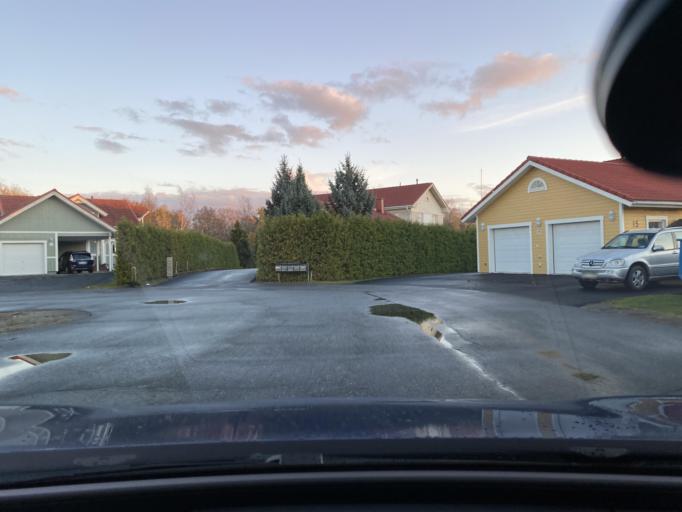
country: FI
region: Satakunta
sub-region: Pori
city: Huittinen
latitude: 61.1805
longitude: 22.7053
